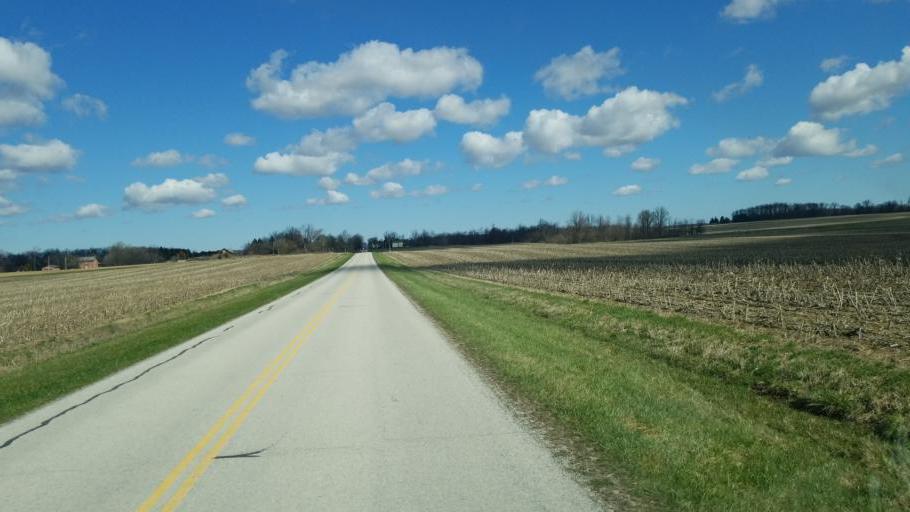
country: US
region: Ohio
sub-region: Sandusky County
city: Mount Carmel
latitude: 41.1571
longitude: -82.9381
